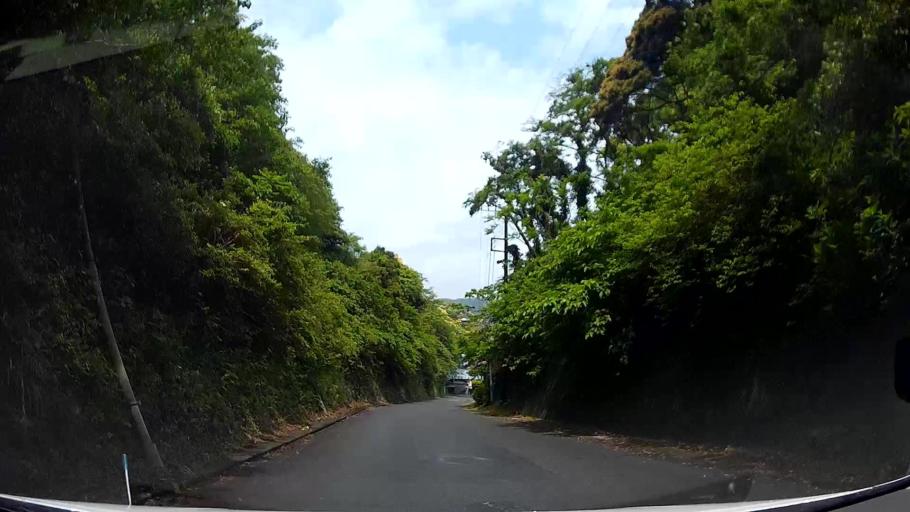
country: JP
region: Shizuoka
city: Shimoda
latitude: 34.6696
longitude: 138.9439
